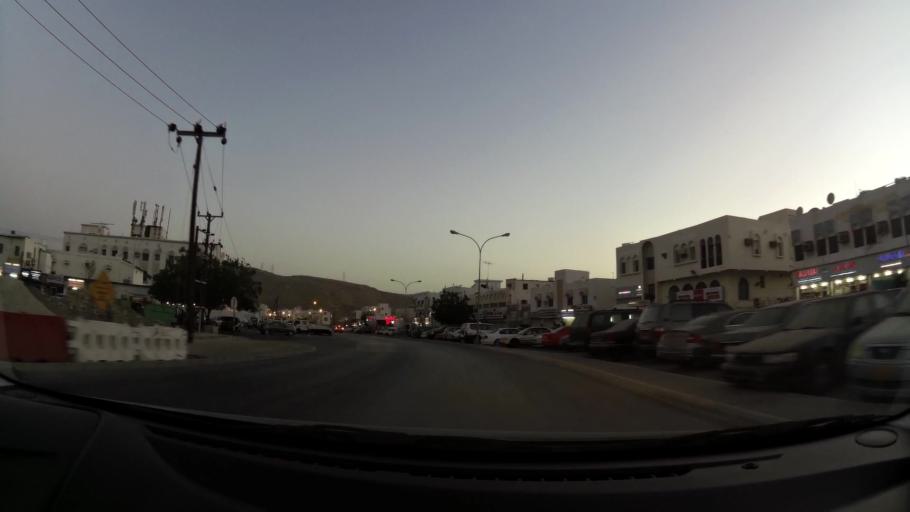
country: OM
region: Muhafazat Masqat
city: Muscat
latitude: 23.5926
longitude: 58.5625
